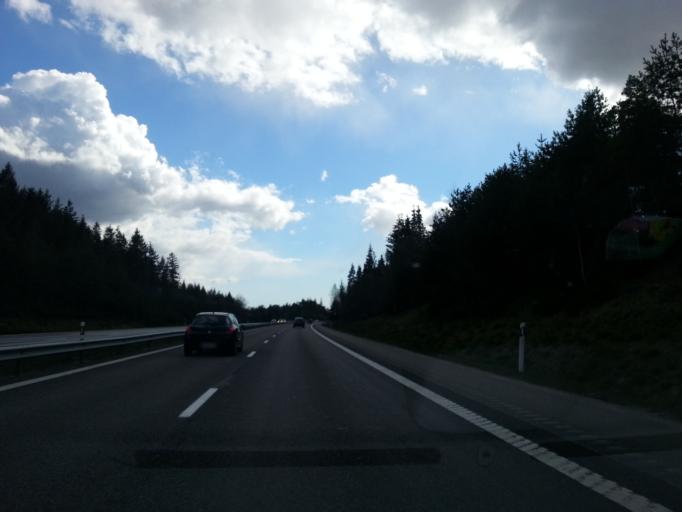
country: SE
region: Vaestra Goetaland
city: Svanesund
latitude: 58.1301
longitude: 11.8854
